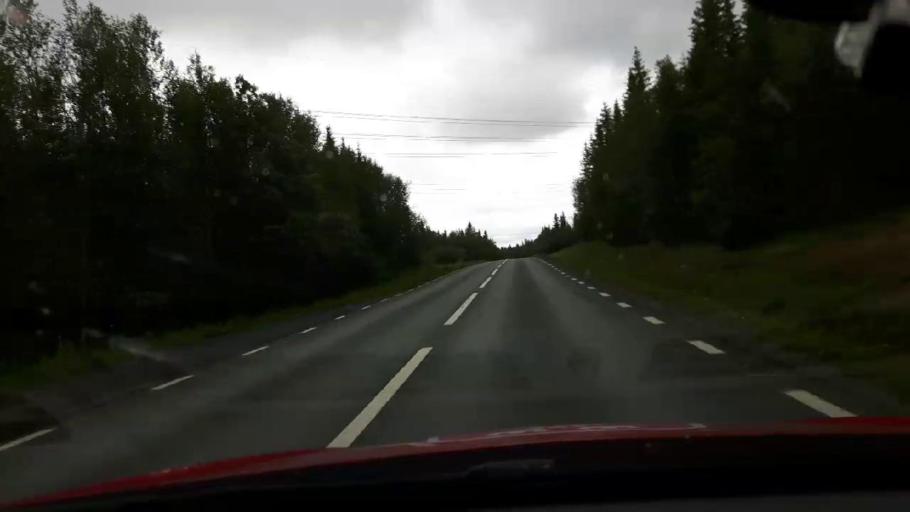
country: SE
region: Jaemtland
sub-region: Are Kommun
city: Are
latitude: 63.3382
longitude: 12.5641
